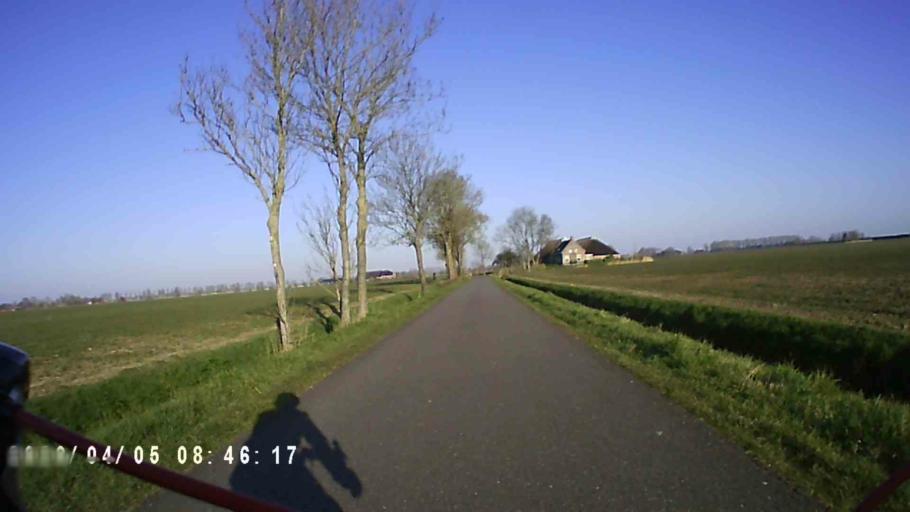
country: NL
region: Groningen
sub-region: Gemeente Winsum
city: Winsum
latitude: 53.3110
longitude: 6.4846
